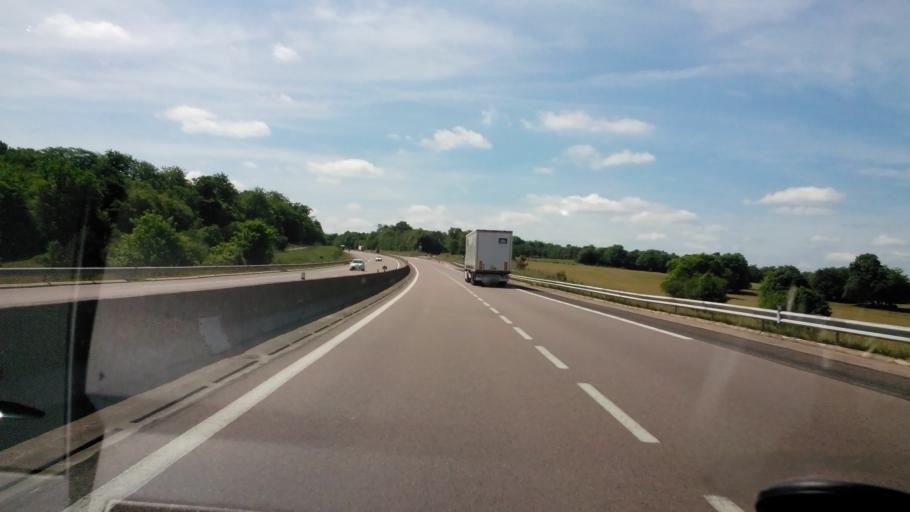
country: FR
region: Lorraine
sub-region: Departement de Meurthe-et-Moselle
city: Colombey-les-Belles
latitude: 48.4325
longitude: 5.8605
